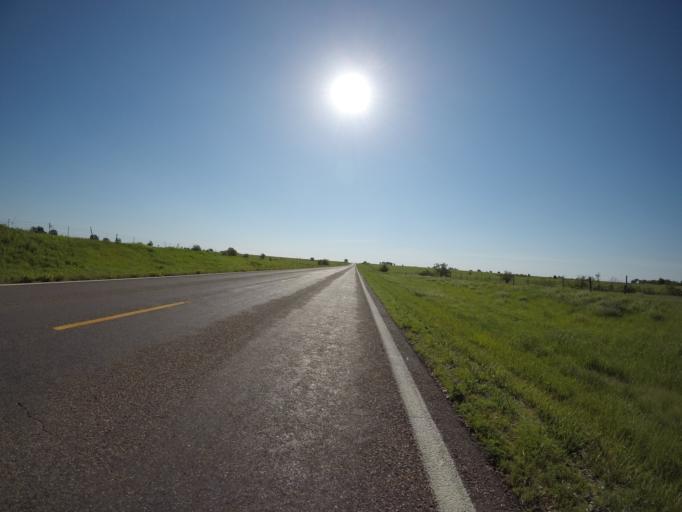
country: US
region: Kansas
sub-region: Lyon County
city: Emporia
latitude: 38.6587
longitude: -96.1975
